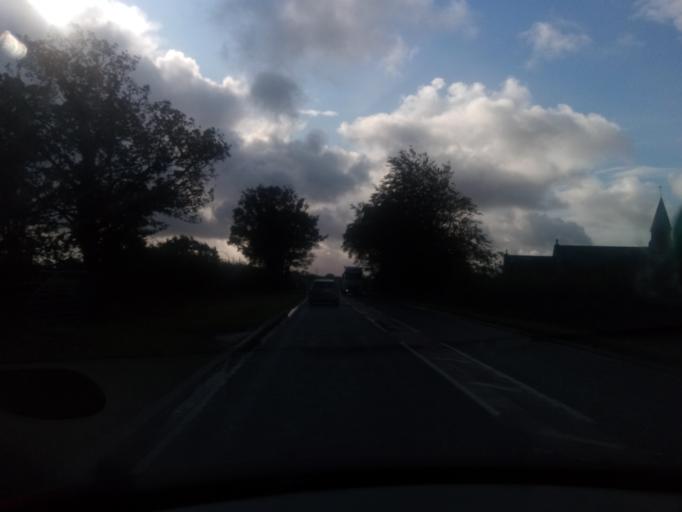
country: GB
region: England
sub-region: Cumbria
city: Carlisle
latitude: 54.9540
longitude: -2.9438
